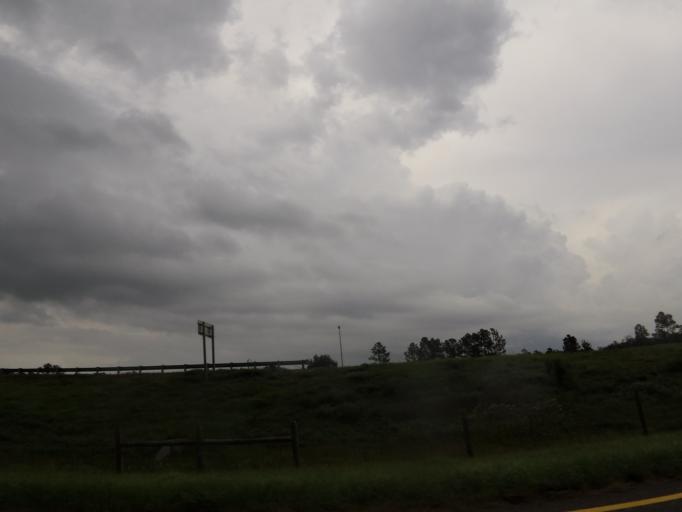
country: US
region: Florida
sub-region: Clay County
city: Lakeside
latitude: 30.1290
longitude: -81.8312
